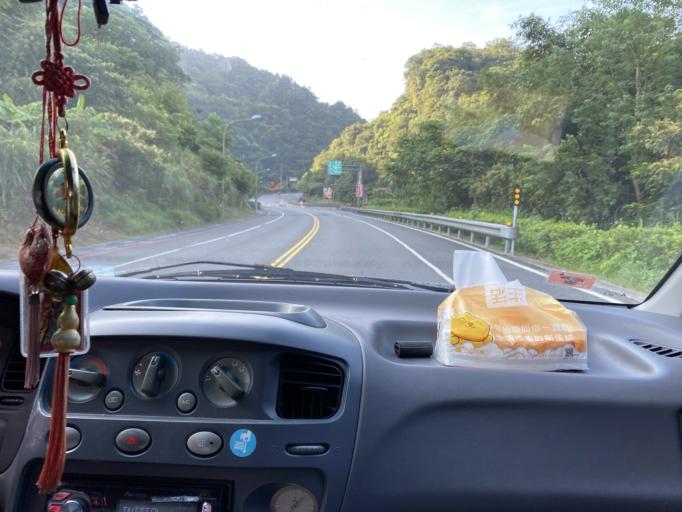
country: TW
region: Taiwan
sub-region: Keelung
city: Keelung
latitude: 25.0408
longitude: 121.7798
